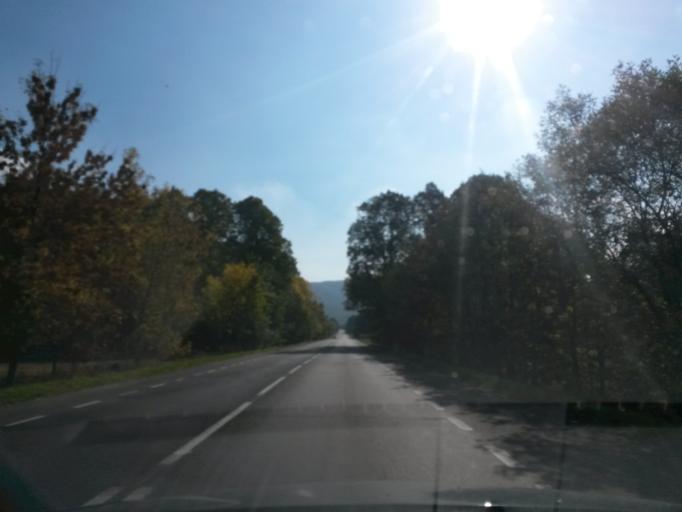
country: PL
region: Lower Silesian Voivodeship
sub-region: Powiat jeleniogorski
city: Kowary
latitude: 50.7990
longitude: 15.8419
